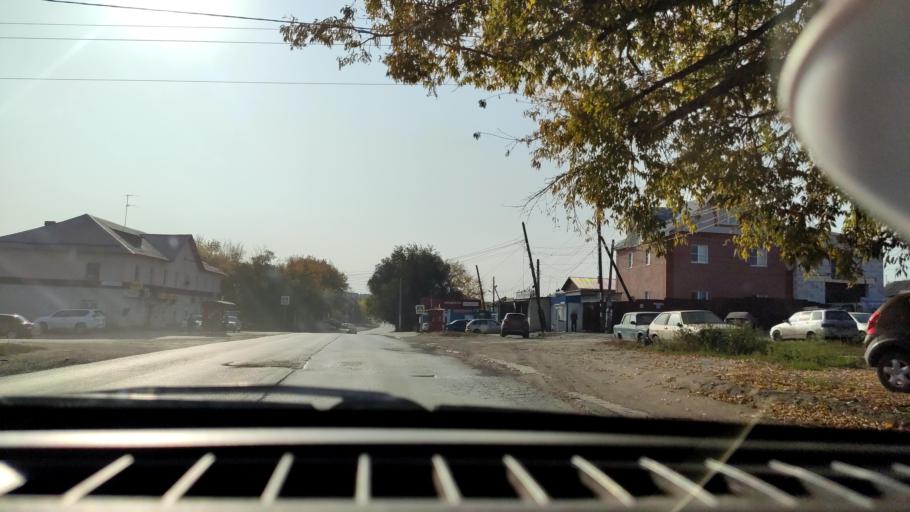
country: RU
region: Samara
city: Samara
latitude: 53.1759
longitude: 50.1802
